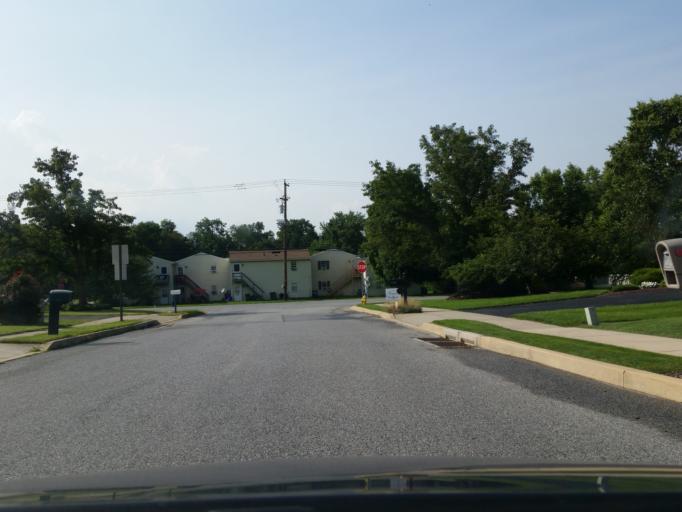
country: US
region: Pennsylvania
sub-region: York County
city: Weigelstown
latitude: 39.9803
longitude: -76.8346
